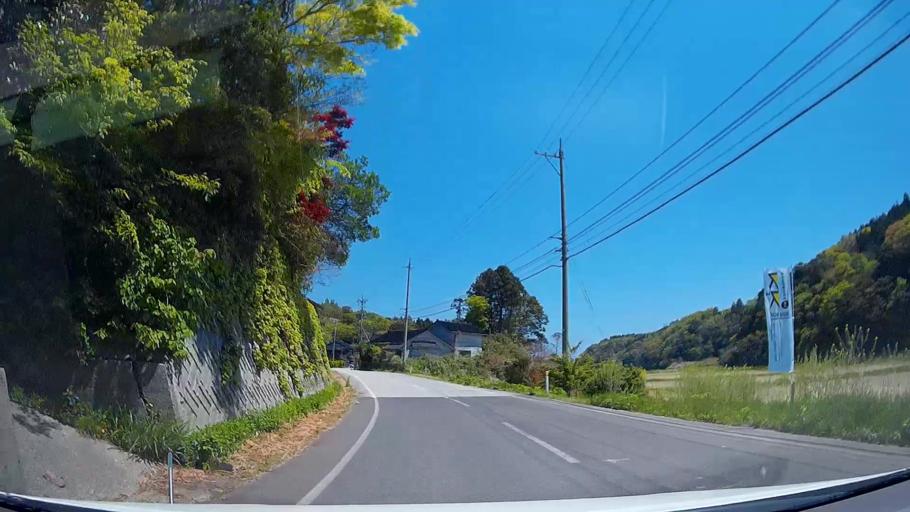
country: JP
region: Ishikawa
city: Nanao
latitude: 37.5245
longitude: 137.3106
